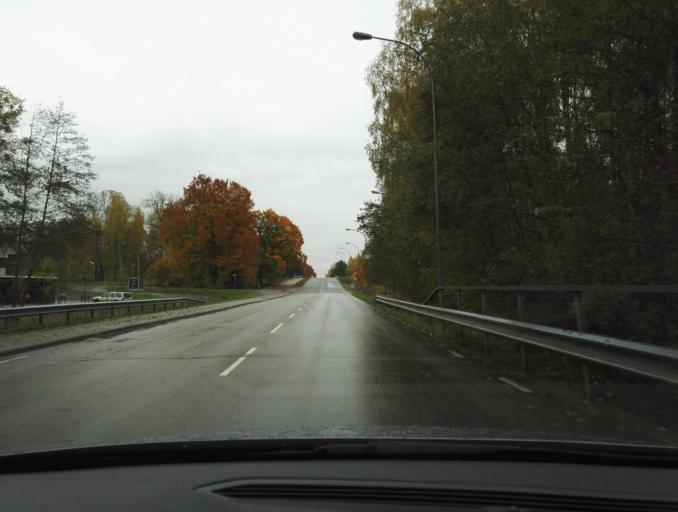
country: SE
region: Kronoberg
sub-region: Vaxjo Kommun
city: Vaexjoe
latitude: 56.8891
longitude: 14.7459
